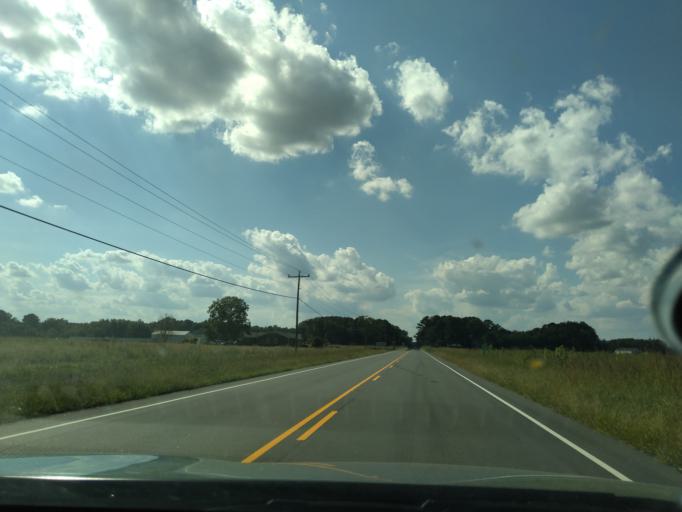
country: US
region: North Carolina
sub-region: Martin County
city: Robersonville
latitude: 35.8223
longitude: -77.3048
